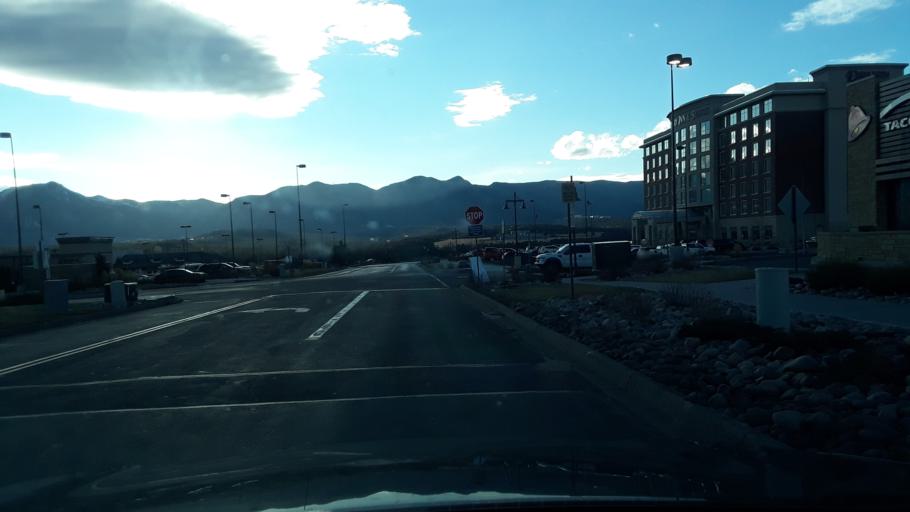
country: US
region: Colorado
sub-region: El Paso County
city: Gleneagle
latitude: 38.9921
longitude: -104.8072
